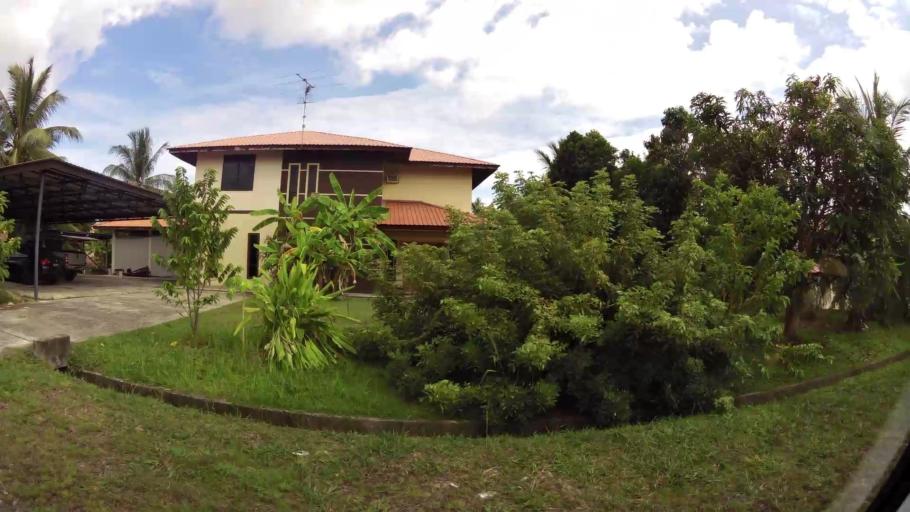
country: BN
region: Brunei and Muara
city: Bandar Seri Begawan
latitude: 4.9381
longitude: 114.9005
